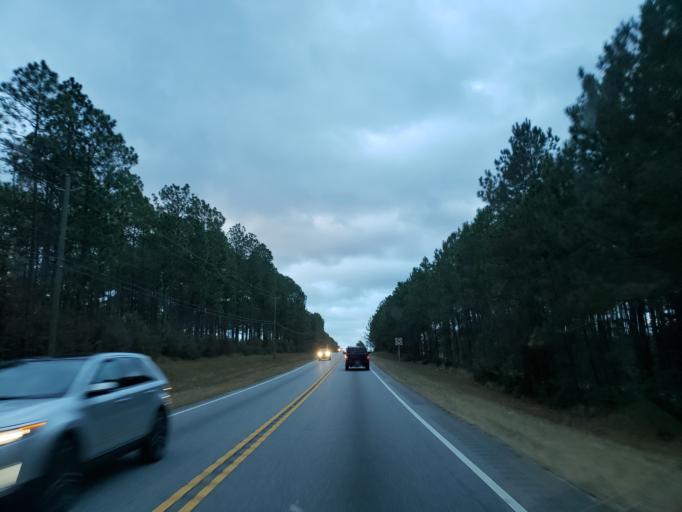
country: US
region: Alabama
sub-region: Mobile County
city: Chickasaw
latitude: 30.7871
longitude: -88.2857
